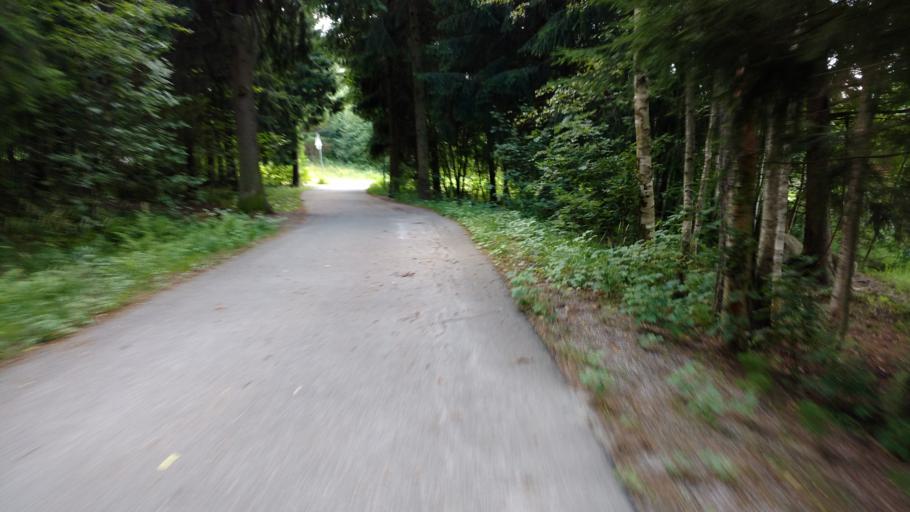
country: FI
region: Varsinais-Suomi
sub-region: Salo
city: Salo
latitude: 60.4029
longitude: 23.1742
